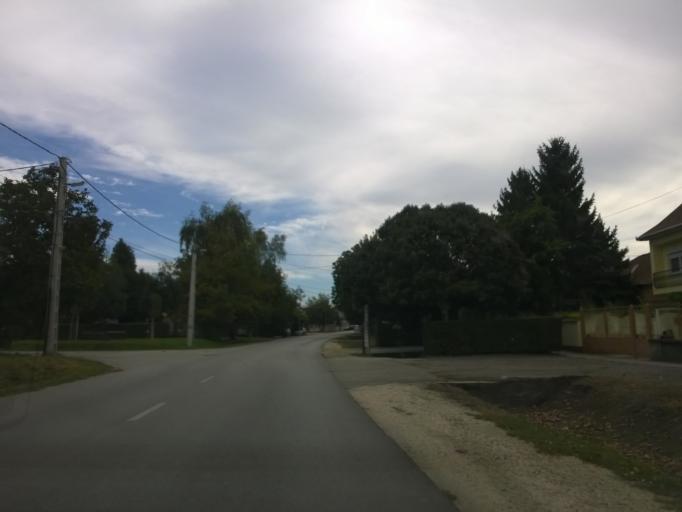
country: HU
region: Pest
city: Szigetszentmiklos
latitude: 47.3526
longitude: 19.0391
